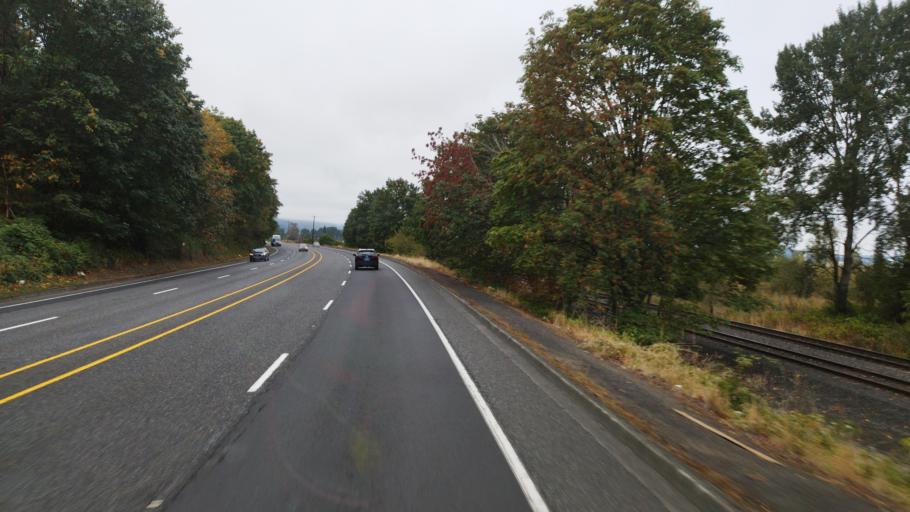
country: US
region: Oregon
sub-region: Columbia County
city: Rainier
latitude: 46.0929
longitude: -122.9468
